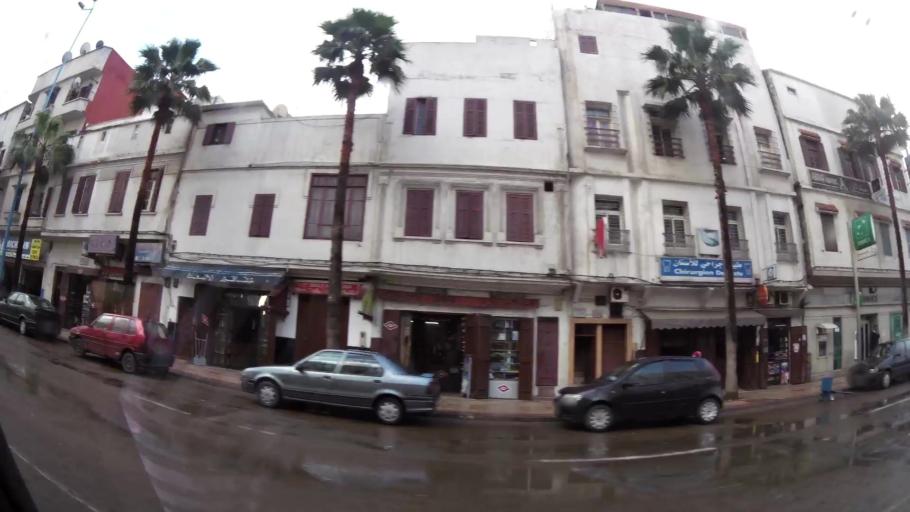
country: MA
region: Grand Casablanca
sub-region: Casablanca
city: Casablanca
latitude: 33.5709
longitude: -7.5968
